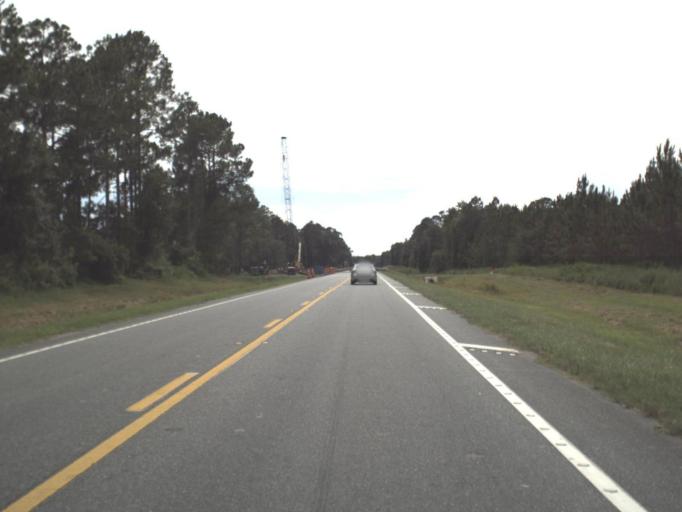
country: US
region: Florida
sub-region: Taylor County
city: Perry
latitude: 30.0987
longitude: -83.4685
